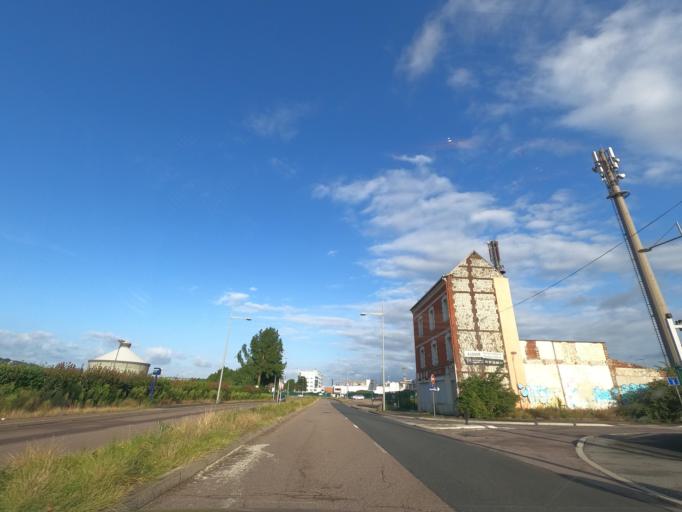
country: FR
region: Haute-Normandie
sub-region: Departement de la Seine-Maritime
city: Le Petit-Quevilly
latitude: 49.4374
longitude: 1.0552
